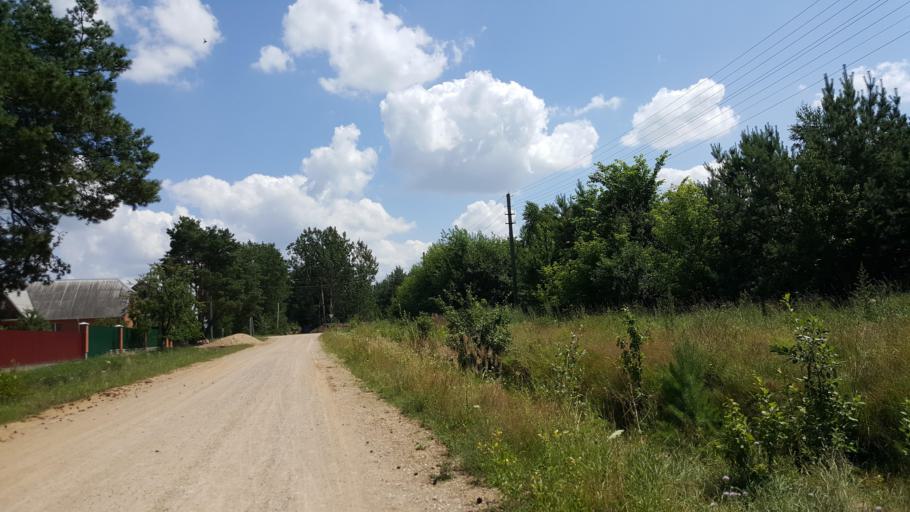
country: BY
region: Brest
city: Kamyanyets
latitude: 52.4004
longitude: 23.8455
